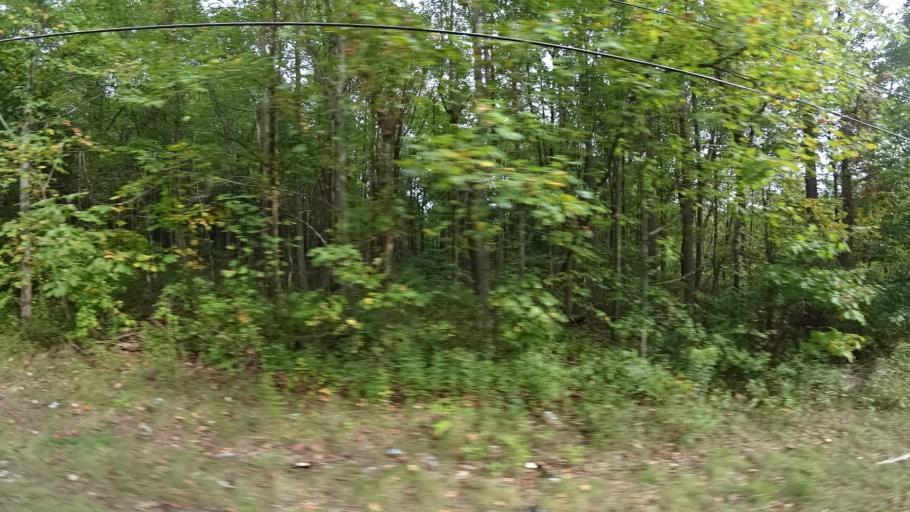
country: US
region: Indiana
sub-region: LaPorte County
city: Long Beach
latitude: 41.7264
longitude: -86.8162
